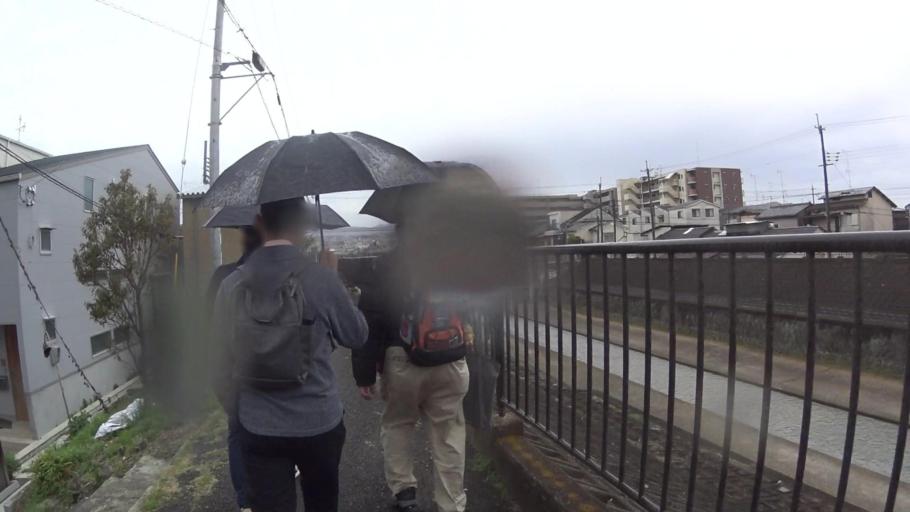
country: JP
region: Kyoto
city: Muko
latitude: 34.9433
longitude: 135.7565
